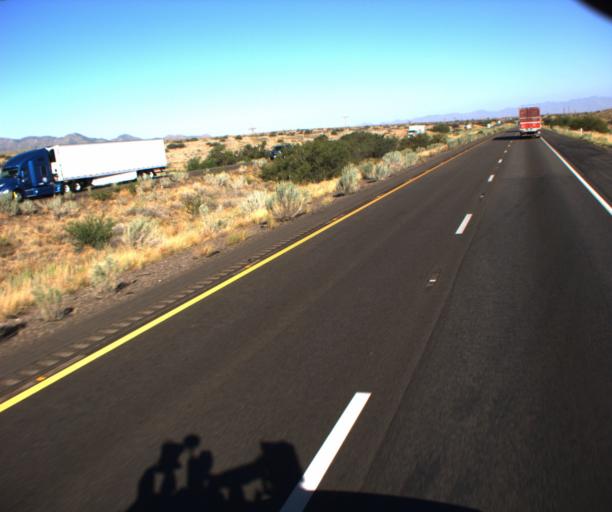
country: US
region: Arizona
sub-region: Mohave County
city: New Kingman-Butler
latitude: 35.1855
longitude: -113.8094
